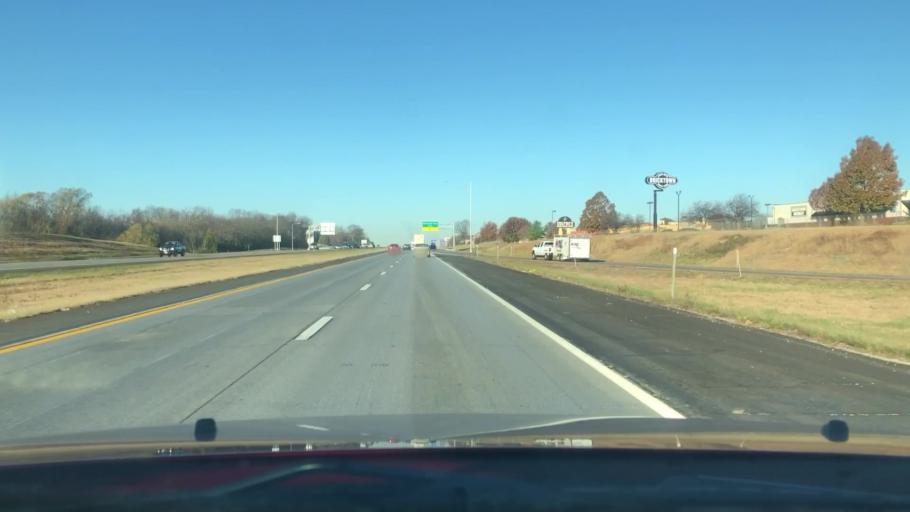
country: US
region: Missouri
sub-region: Greene County
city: Springfield
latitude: 37.1398
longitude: -93.2559
